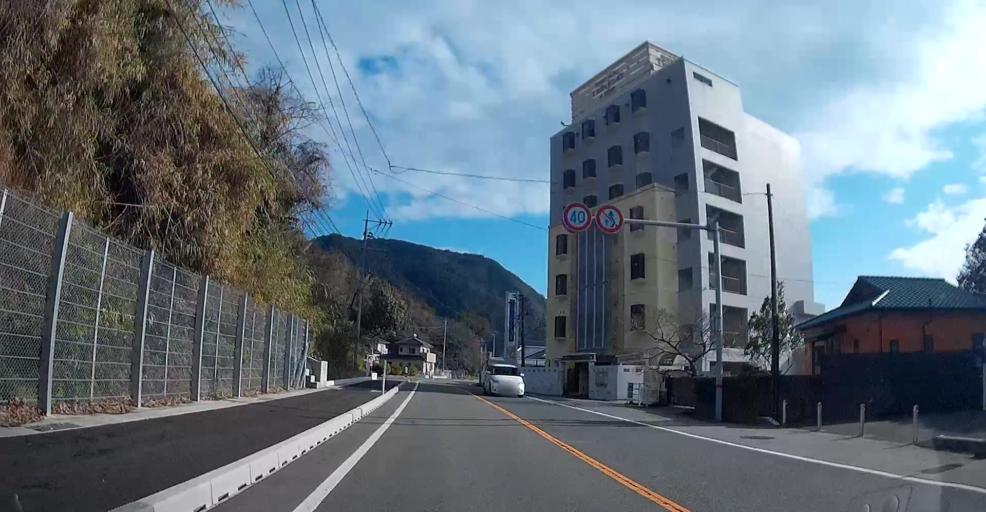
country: JP
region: Kumamoto
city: Yatsushiro
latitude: 32.6203
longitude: 130.4583
